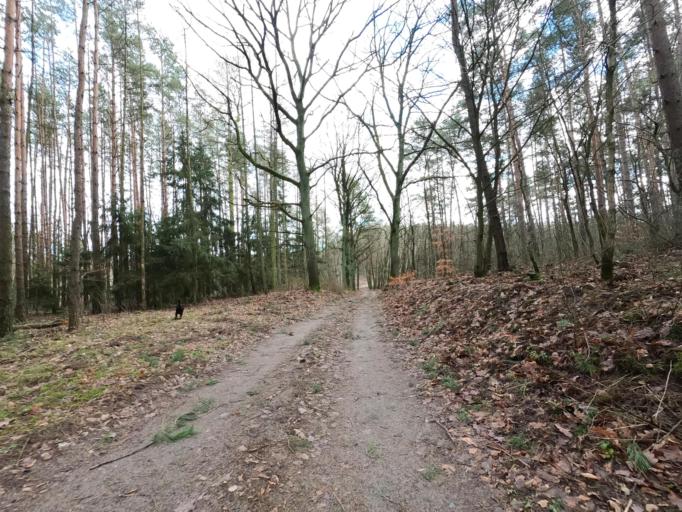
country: PL
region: Greater Poland Voivodeship
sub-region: Powiat pilski
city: Bialosliwie
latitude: 53.1038
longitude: 17.0767
